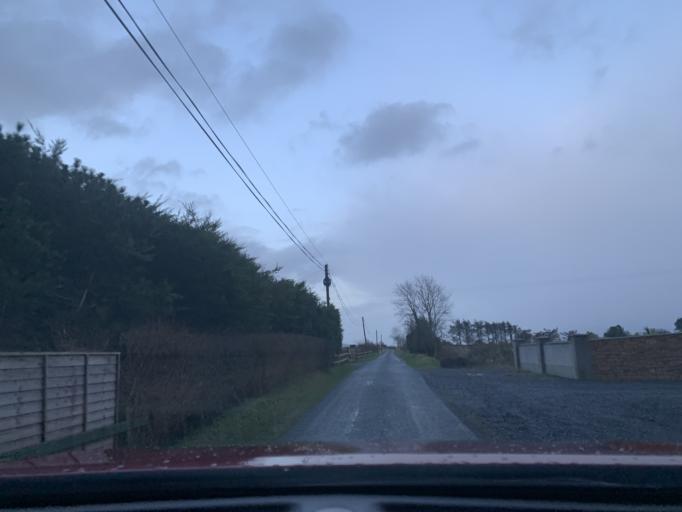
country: IE
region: Connaught
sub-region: Roscommon
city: Ballaghaderreen
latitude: 53.9797
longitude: -8.5493
